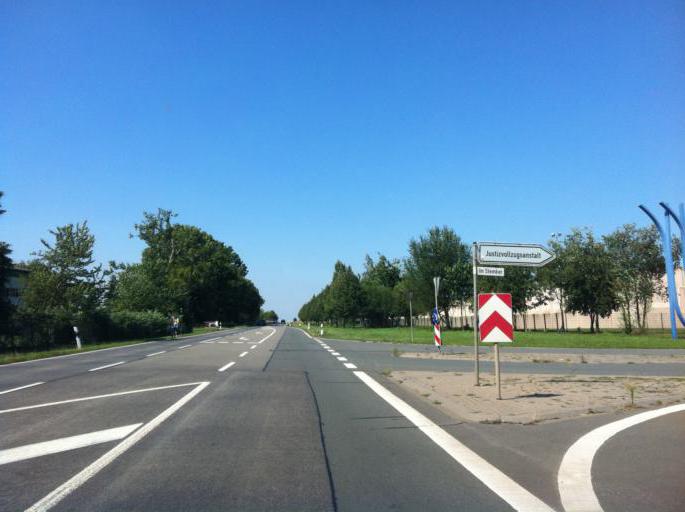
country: DE
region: Thuringia
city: Ballstadt
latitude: 51.0928
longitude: 10.7223
